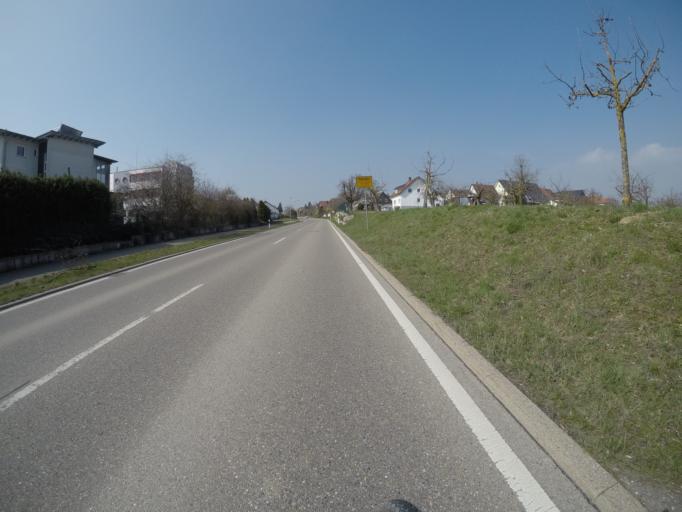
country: DE
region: Baden-Wuerttemberg
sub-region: Regierungsbezirk Stuttgart
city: Herrenberg
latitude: 48.6145
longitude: 8.8478
